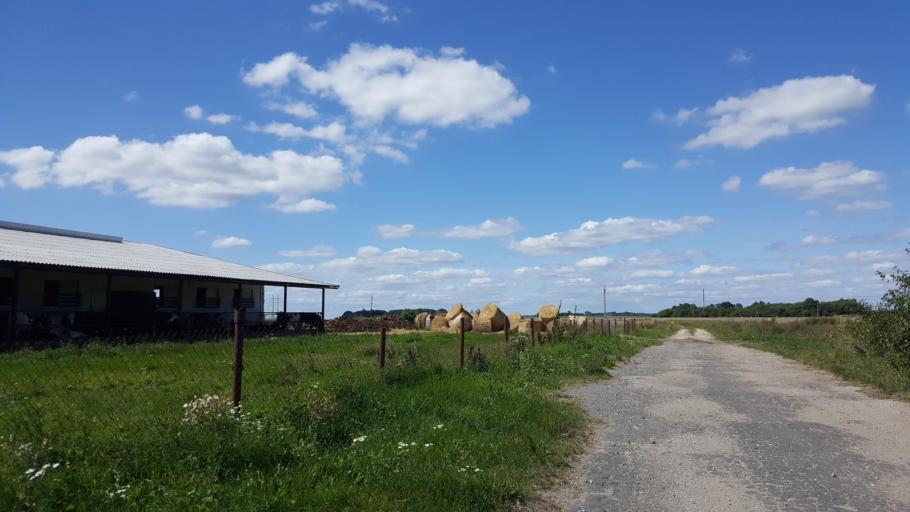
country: BY
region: Brest
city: Kobryn
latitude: 52.2973
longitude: 24.3315
